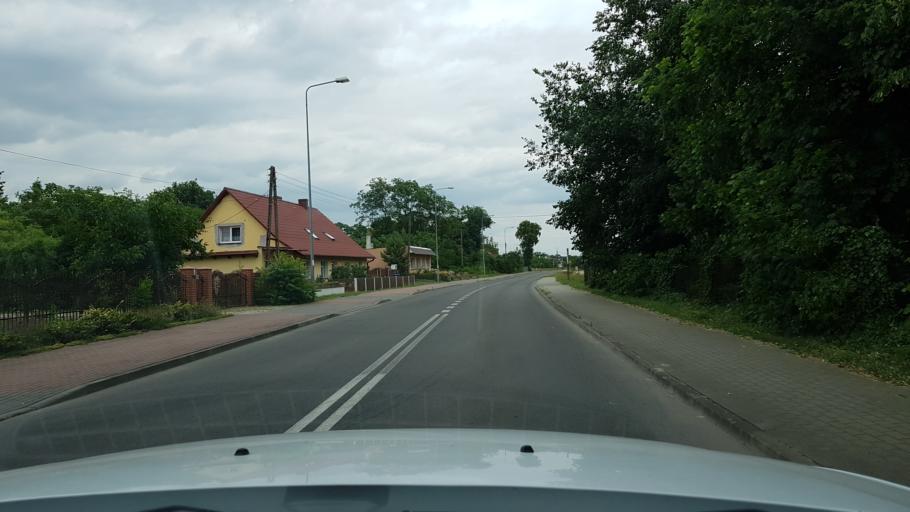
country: PL
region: Lubusz
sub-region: Powiat gorzowski
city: Kostrzyn nad Odra
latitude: 52.6229
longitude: 14.5829
